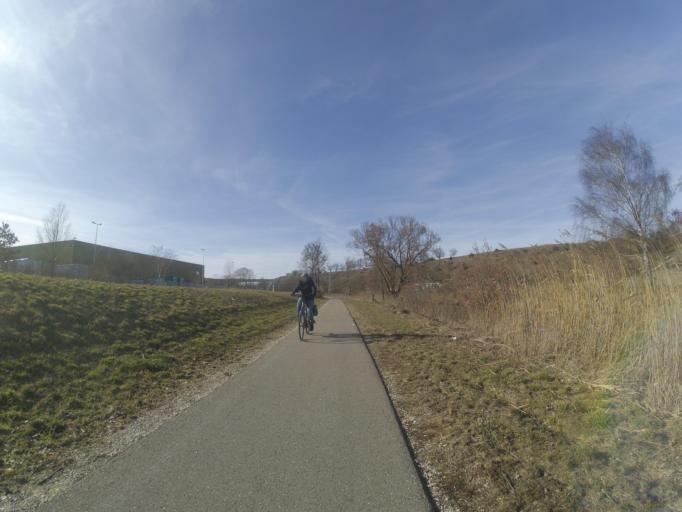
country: DE
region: Baden-Wuerttemberg
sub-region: Regierungsbezirk Stuttgart
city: Giengen an der Brenz
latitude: 48.6253
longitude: 10.2302
